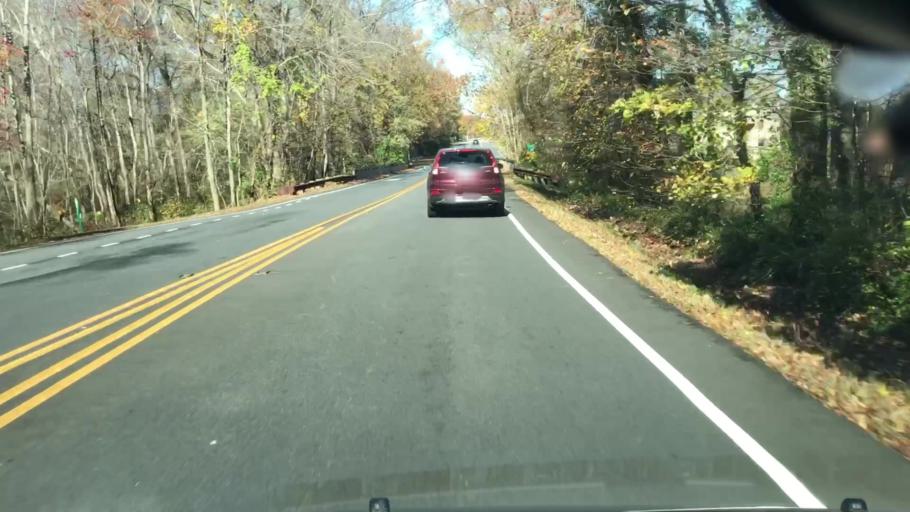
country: US
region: Virginia
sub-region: Fairfax County
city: Woodlawn
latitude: 38.7117
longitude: -77.1296
